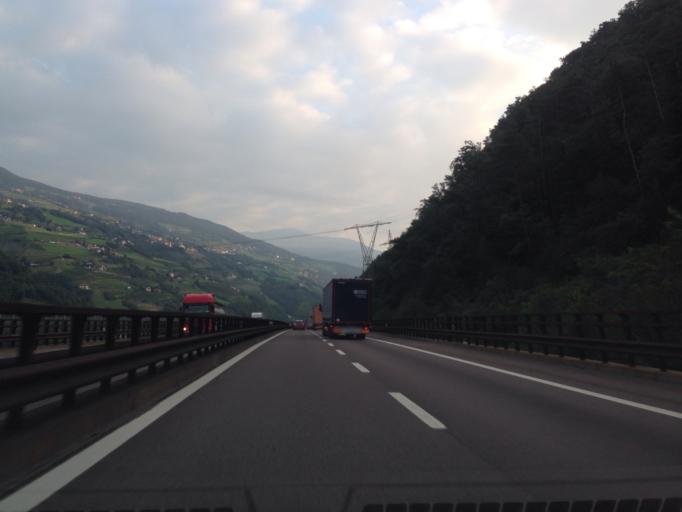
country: IT
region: Trentino-Alto Adige
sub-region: Bolzano
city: Ponte Gardena
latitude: 46.6071
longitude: 11.5356
